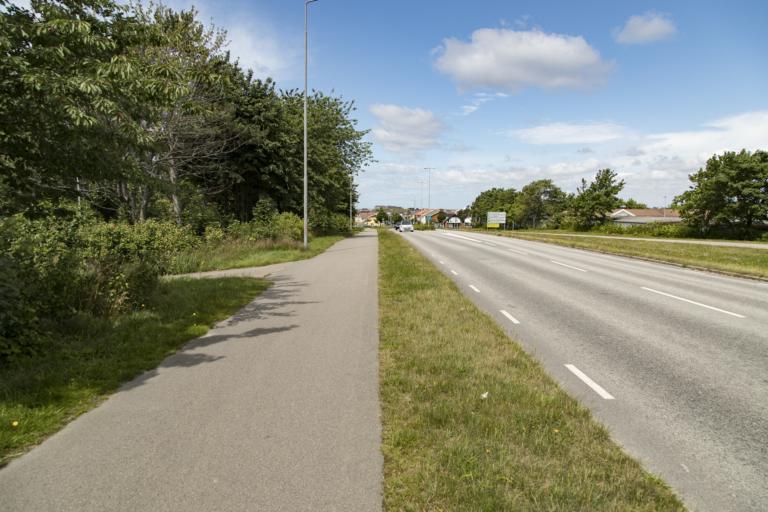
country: SE
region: Halland
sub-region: Varbergs Kommun
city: Varberg
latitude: 57.0933
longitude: 12.2594
